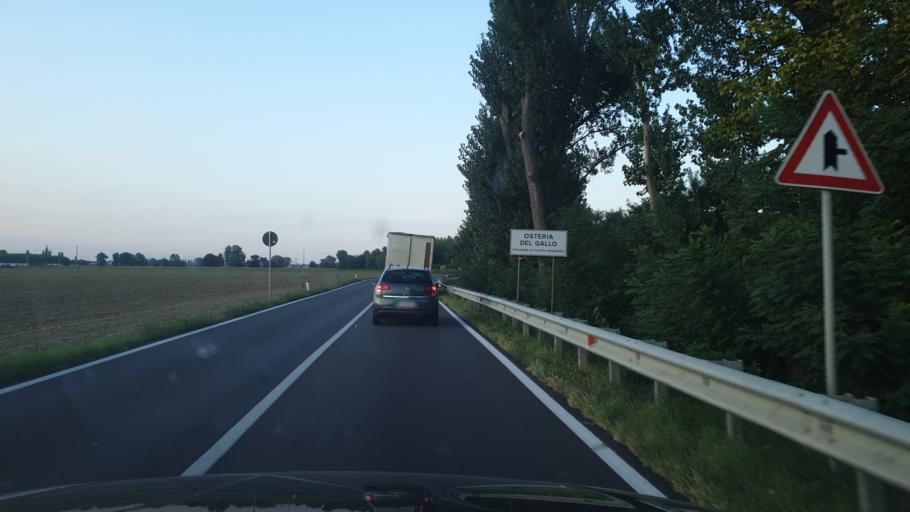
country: IT
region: Emilia-Romagna
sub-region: Provincia di Bologna
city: Progresso
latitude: 44.5582
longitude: 11.3925
